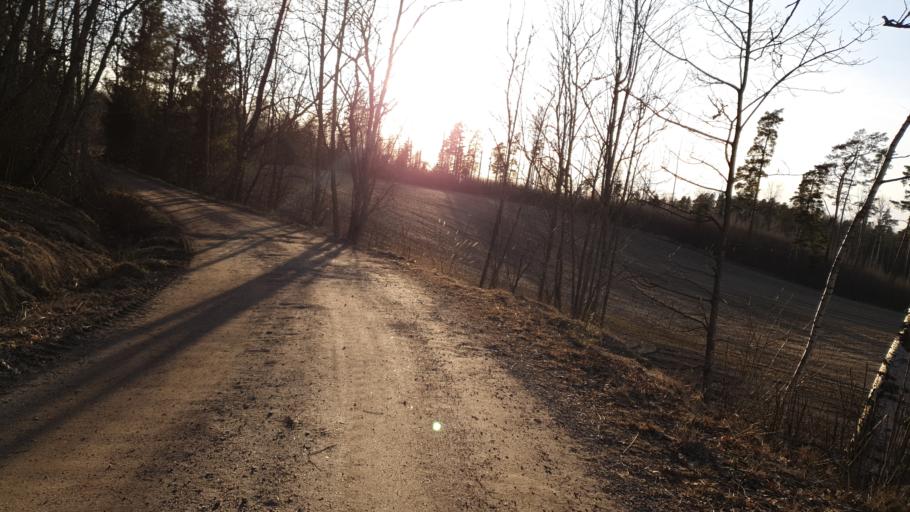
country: FI
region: Uusimaa
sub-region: Helsinki
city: Nurmijaervi
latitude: 60.3409
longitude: 24.8538
